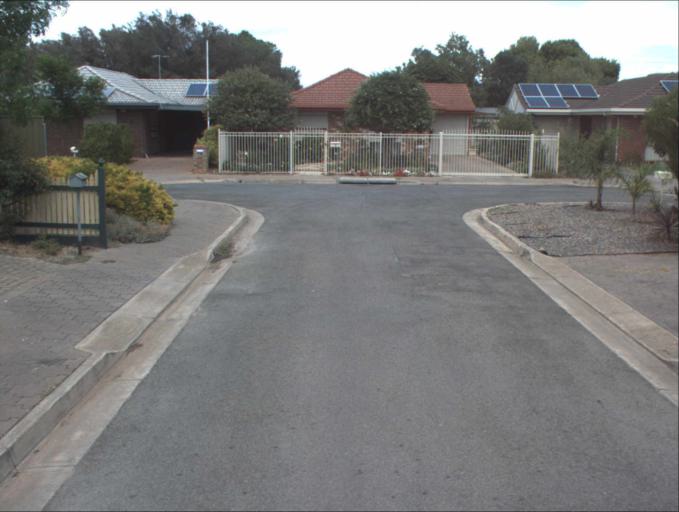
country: AU
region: South Australia
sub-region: Port Adelaide Enfield
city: Enfield
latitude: -34.8590
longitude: 138.6246
